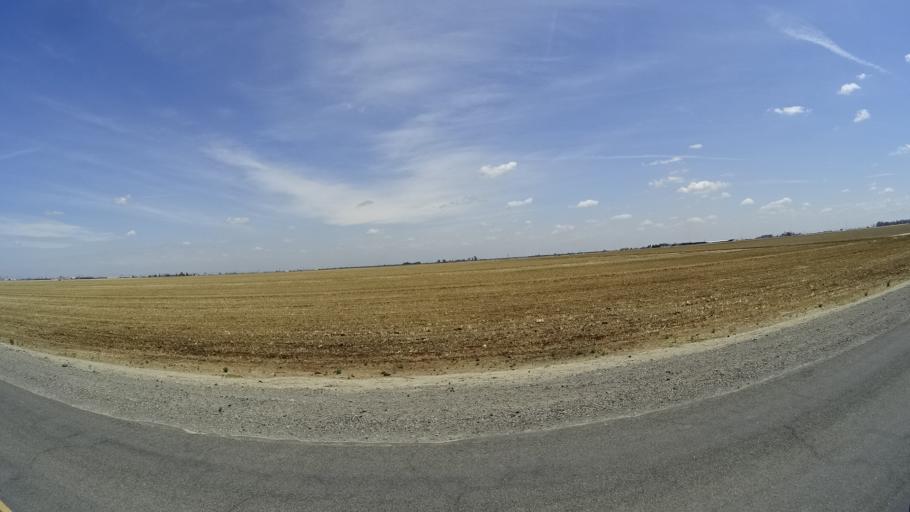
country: US
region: California
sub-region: Kings County
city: Home Garden
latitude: 36.2412
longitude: -119.6728
